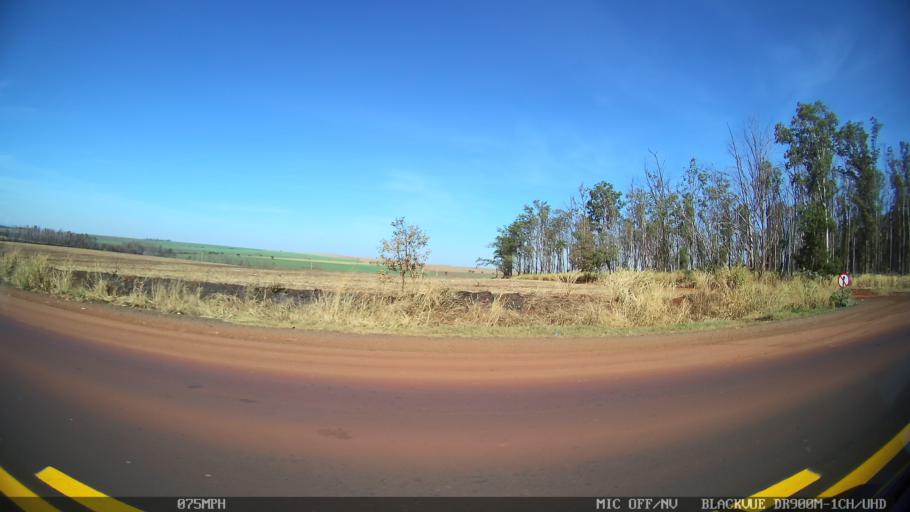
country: BR
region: Sao Paulo
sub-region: Barretos
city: Barretos
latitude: -20.4908
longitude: -48.5223
